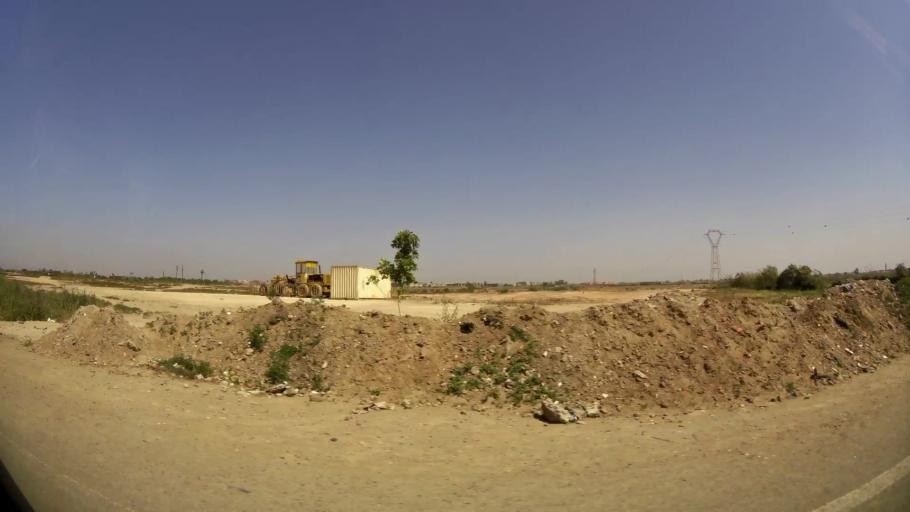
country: MA
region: Souss-Massa-Draa
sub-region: Inezgane-Ait Mellou
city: Inezgane
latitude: 30.3463
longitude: -9.5335
